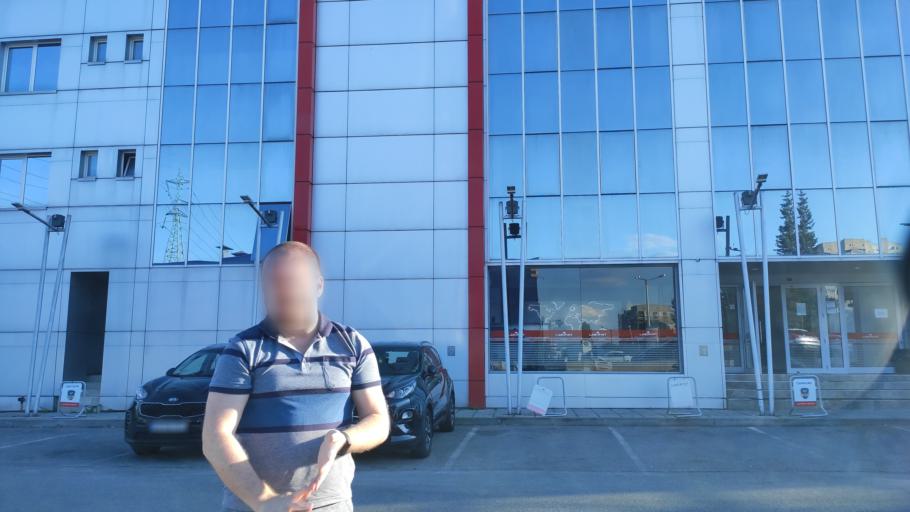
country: BG
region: Sofia-Capital
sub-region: Stolichna Obshtina
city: Sofia
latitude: 42.7116
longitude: 23.2731
